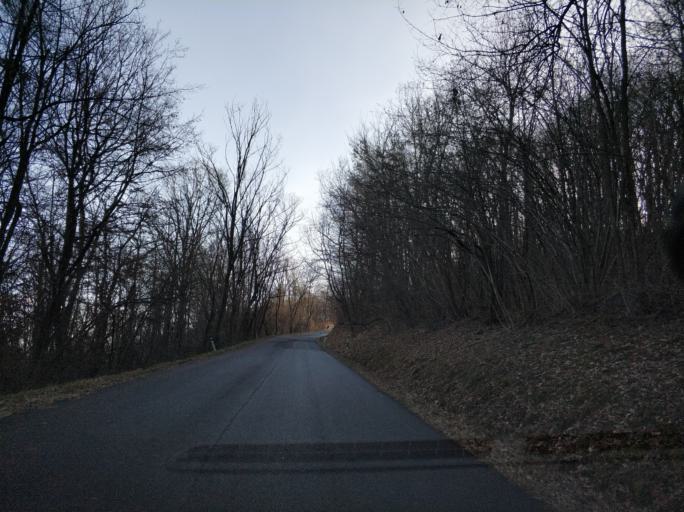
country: IT
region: Piedmont
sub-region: Provincia di Torino
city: Vauda Canavese Superiore
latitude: 45.2681
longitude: 7.6368
